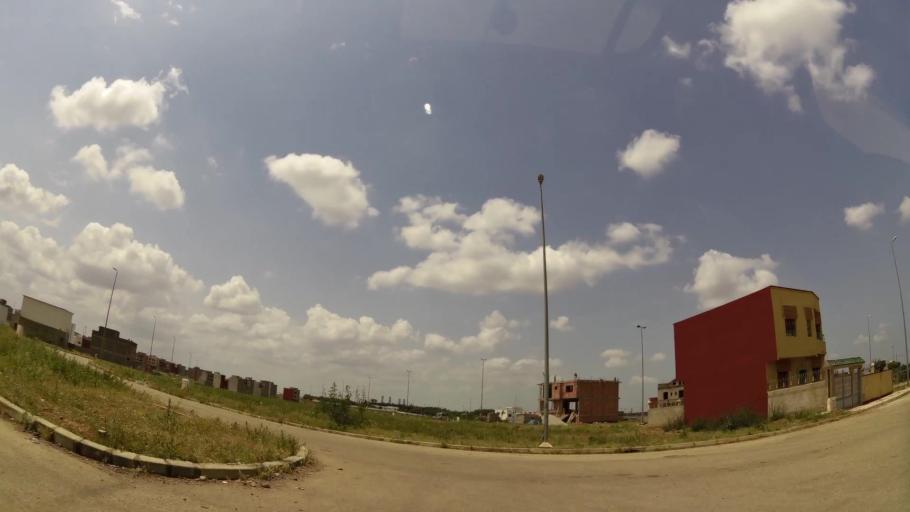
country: MA
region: Rabat-Sale-Zemmour-Zaer
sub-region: Khemisset
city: Tiflet
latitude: 34.0037
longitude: -6.5382
